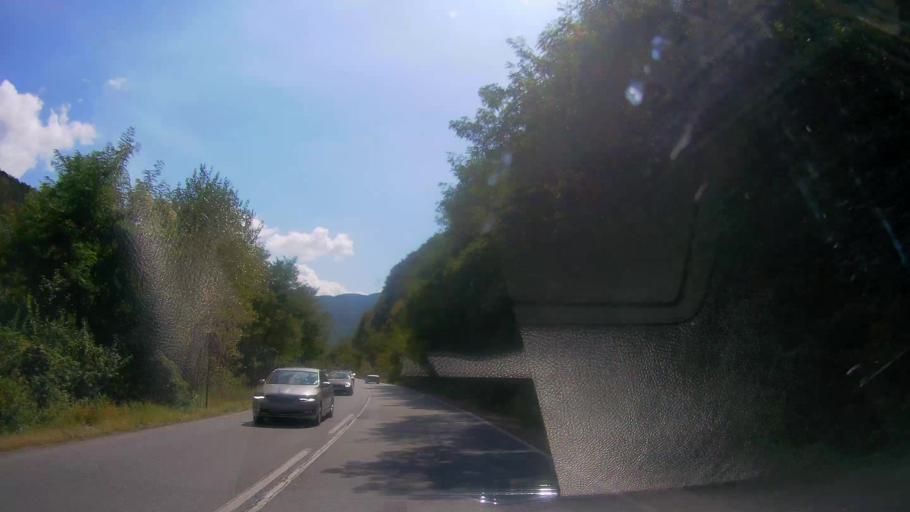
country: BG
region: Stara Zagora
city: Gurkovo
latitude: 42.7256
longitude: 25.7126
